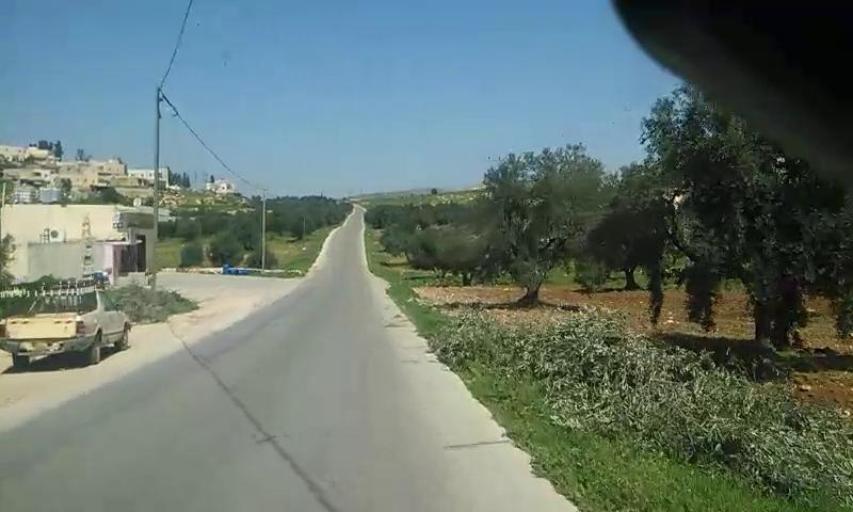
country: PS
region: West Bank
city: Dayr al `Asal al Fawqa
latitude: 31.4711
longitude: 34.9469
